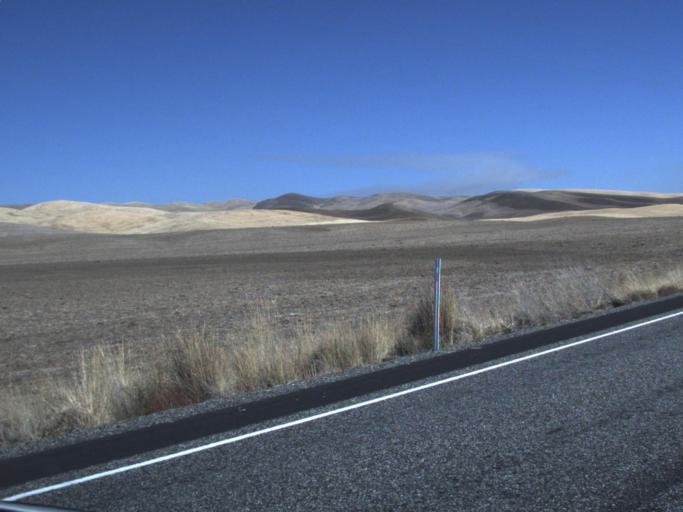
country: US
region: Washington
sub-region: Walla Walla County
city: Waitsburg
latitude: 46.2998
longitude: -118.3731
